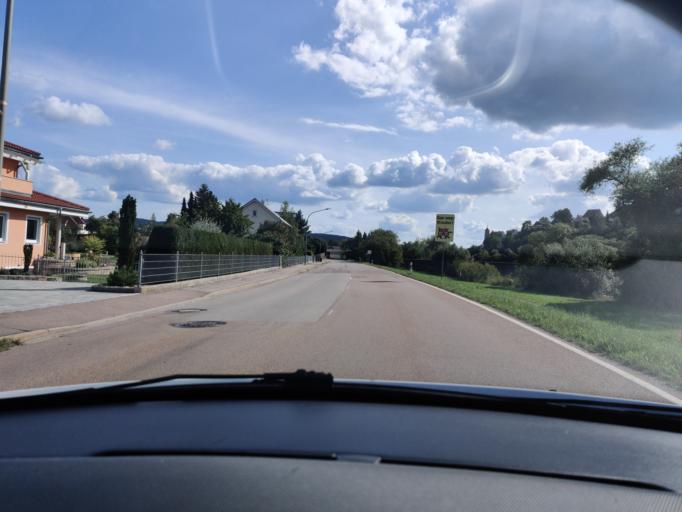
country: DE
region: Bavaria
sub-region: Upper Palatinate
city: Nabburg
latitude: 49.4573
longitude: 12.1844
